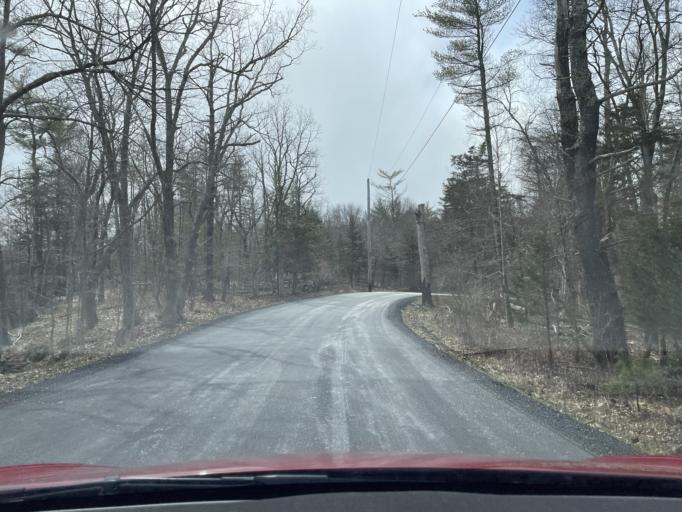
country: US
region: New York
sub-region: Ulster County
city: Manorville
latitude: 42.0867
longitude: -74.0292
